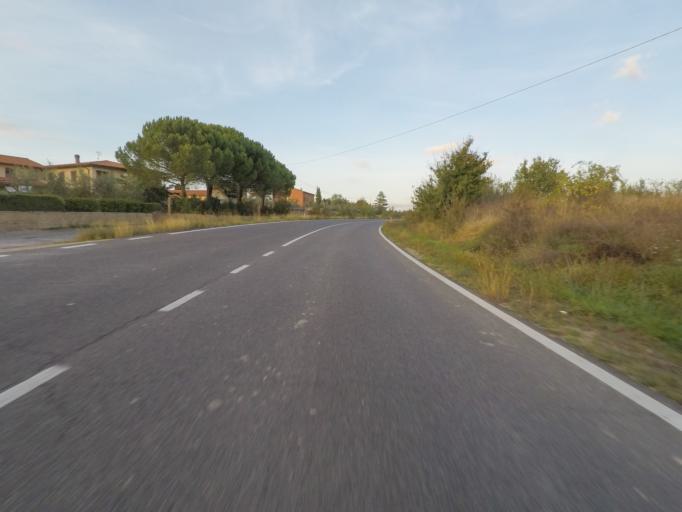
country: IT
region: Tuscany
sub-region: Provincia di Siena
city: Pienza
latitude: 43.0868
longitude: 11.6792
